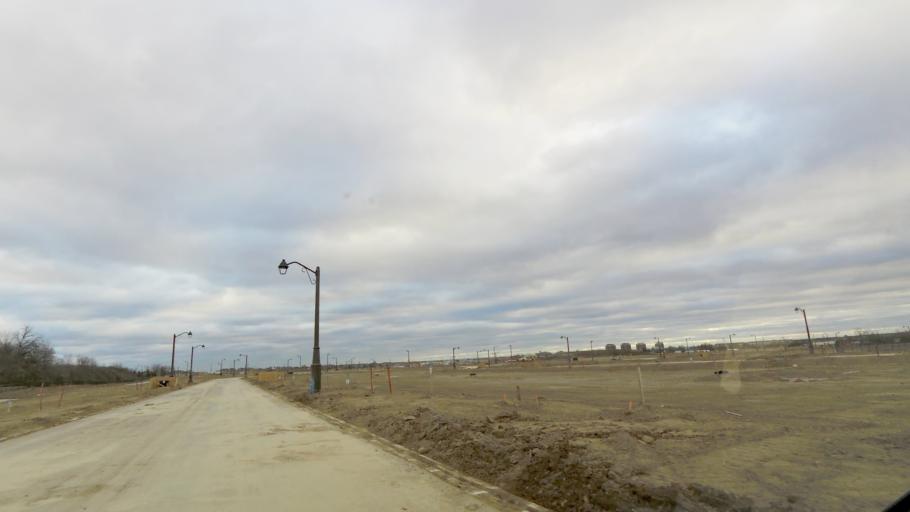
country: CA
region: Ontario
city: Oakville
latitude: 43.4983
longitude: -79.7206
